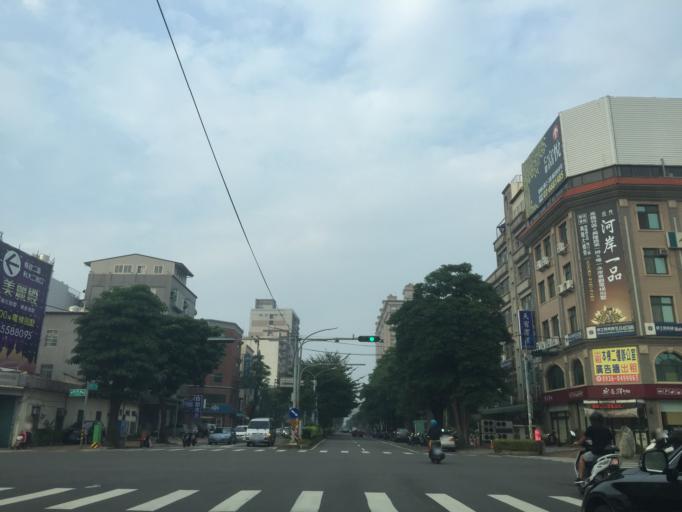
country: TW
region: Taiwan
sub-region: Hsinchu
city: Zhubei
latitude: 24.8212
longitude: 121.0133
